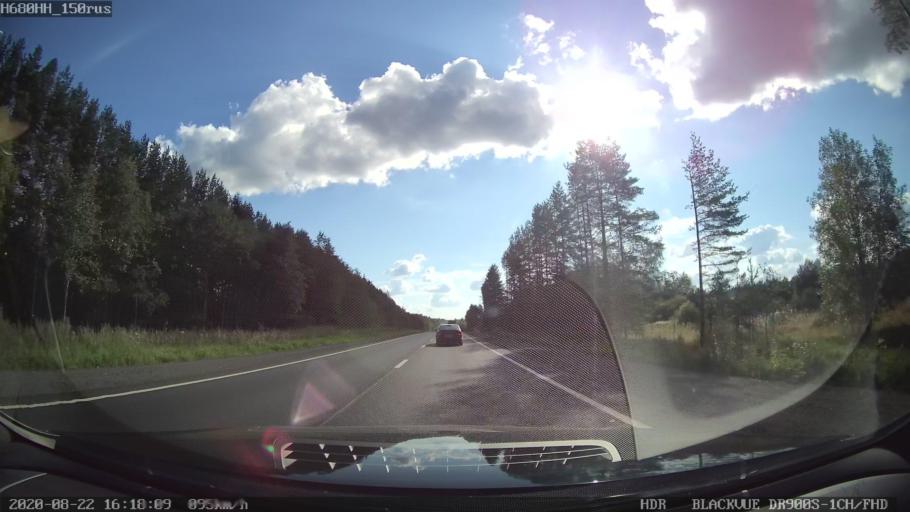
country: RU
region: Tverskaya
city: Rameshki
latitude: 57.4201
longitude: 36.1465
